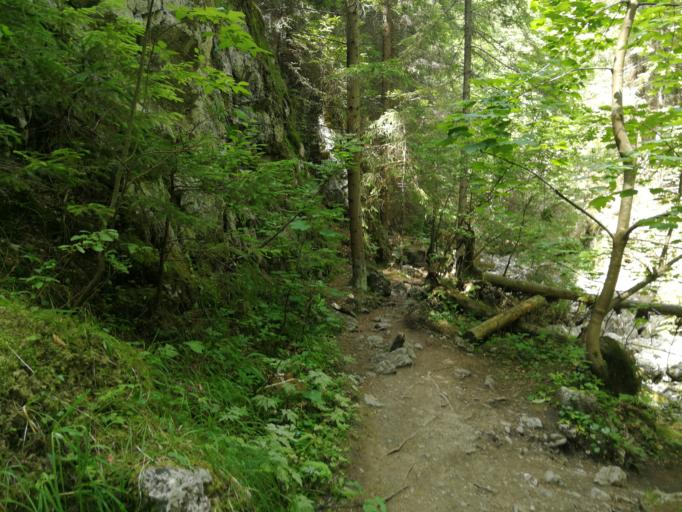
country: SK
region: Zilinsky
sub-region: Okres Liptovsky Mikulas
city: Liptovsky Mikulas
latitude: 49.1629
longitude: 19.4897
